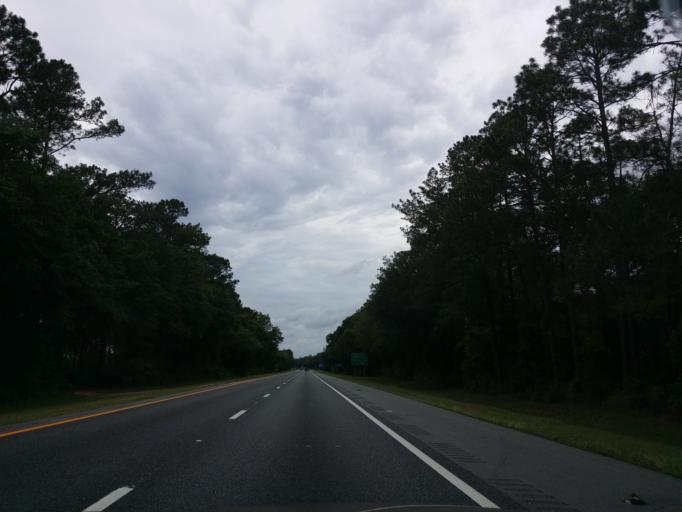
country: US
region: Florida
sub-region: Madison County
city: Madison
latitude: 30.3914
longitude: -83.3369
